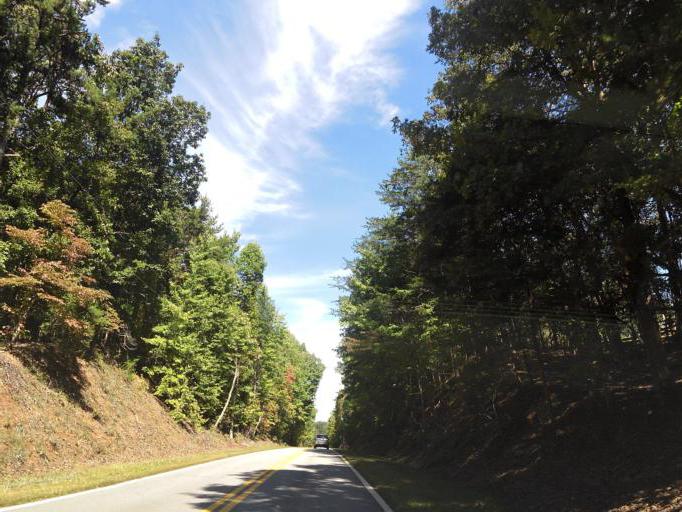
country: US
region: Georgia
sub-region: Pickens County
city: Nelson
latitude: 34.4750
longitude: -84.2585
